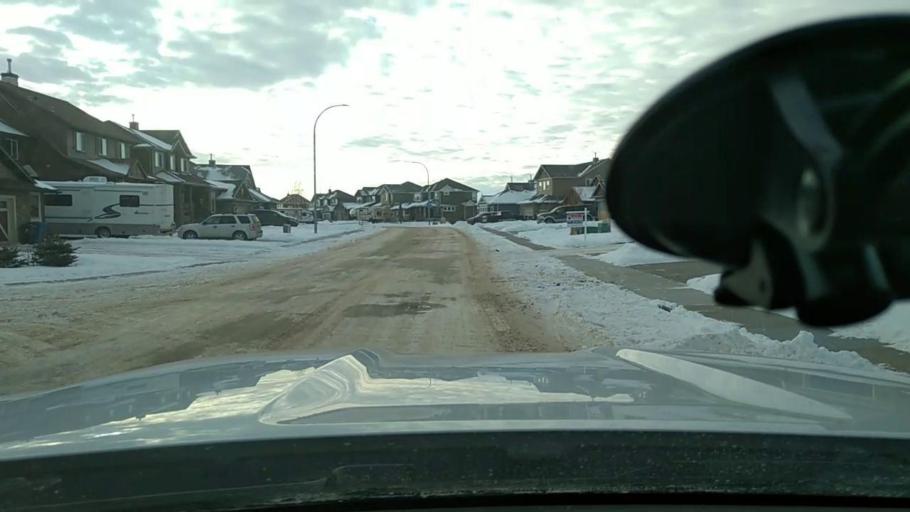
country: CA
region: Alberta
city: Chestermere
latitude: 50.9636
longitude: -113.6628
